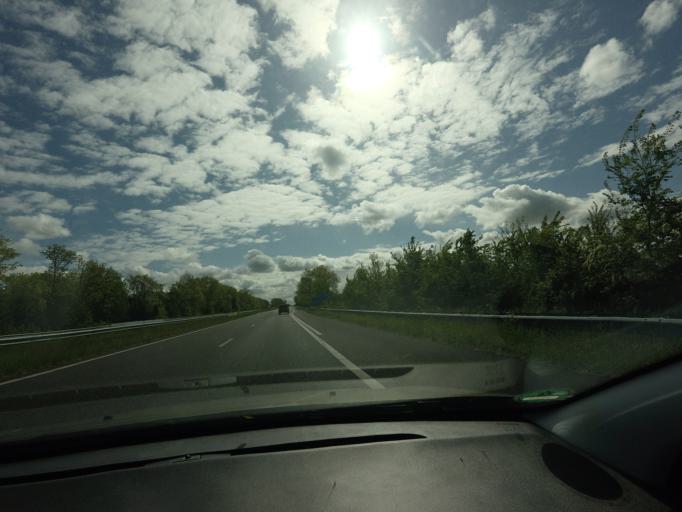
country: NL
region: Friesland
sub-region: Sudwest Fryslan
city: Bolsward
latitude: 53.0572
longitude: 5.5277
